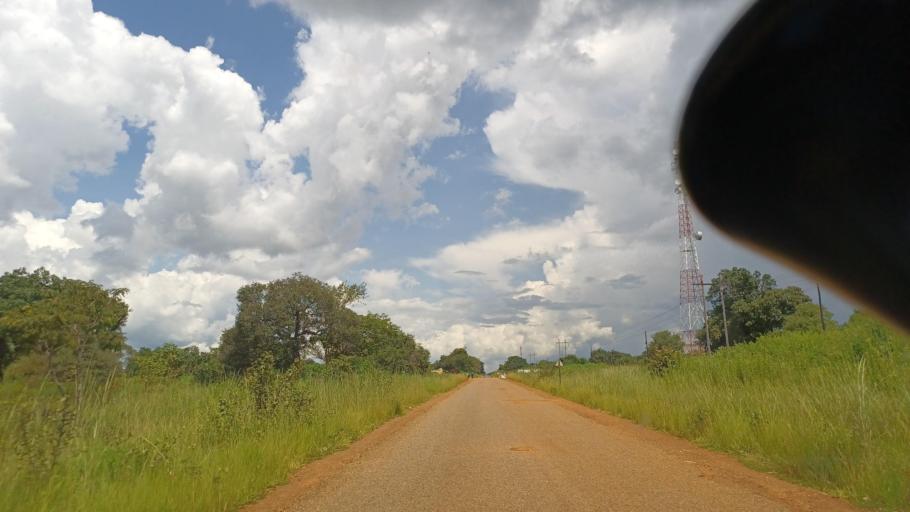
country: ZM
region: North-Western
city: Kasempa
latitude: -12.7842
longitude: 26.0105
